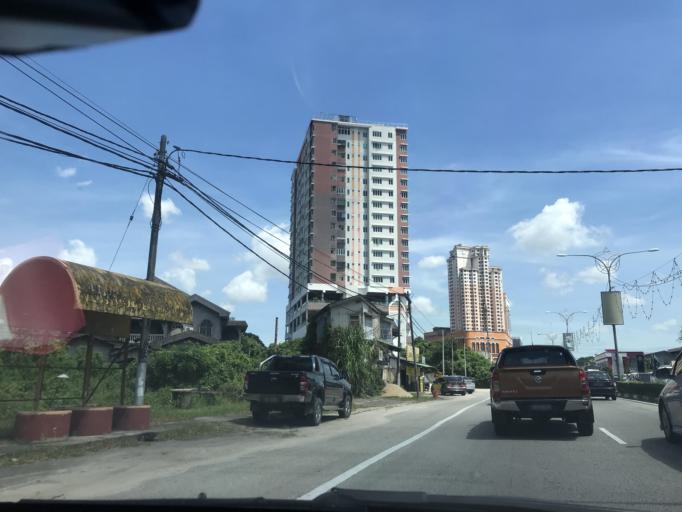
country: MY
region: Kelantan
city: Kota Bharu
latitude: 6.1103
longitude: 102.2538
